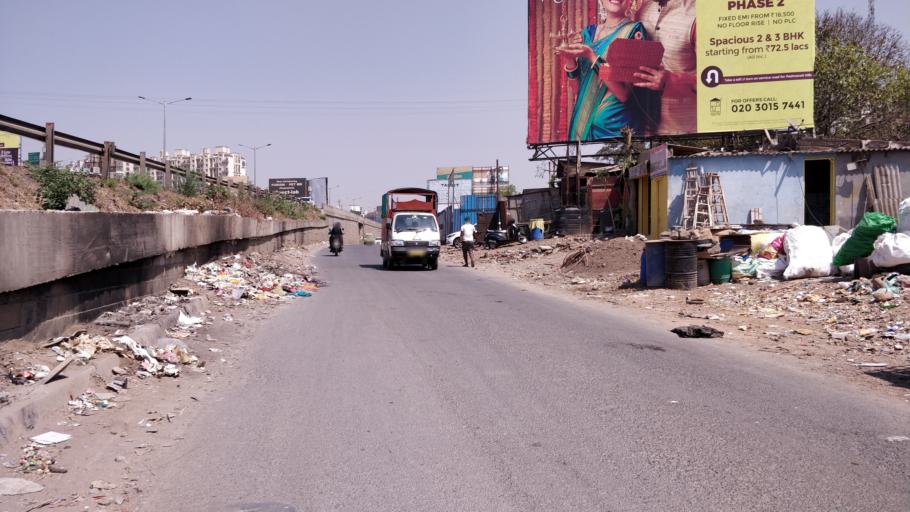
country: IN
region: Maharashtra
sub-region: Pune Division
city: Kharakvasla
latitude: 18.5145
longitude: 73.7696
